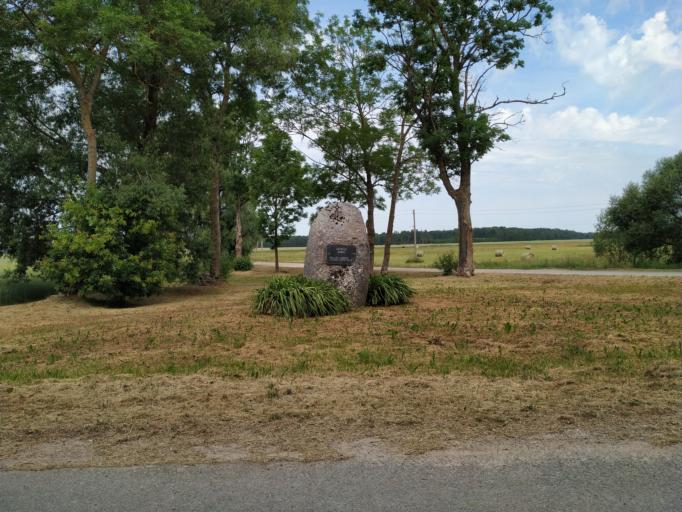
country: LT
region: Panevezys
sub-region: Birzai
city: Birzai
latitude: 56.2752
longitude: 24.5990
